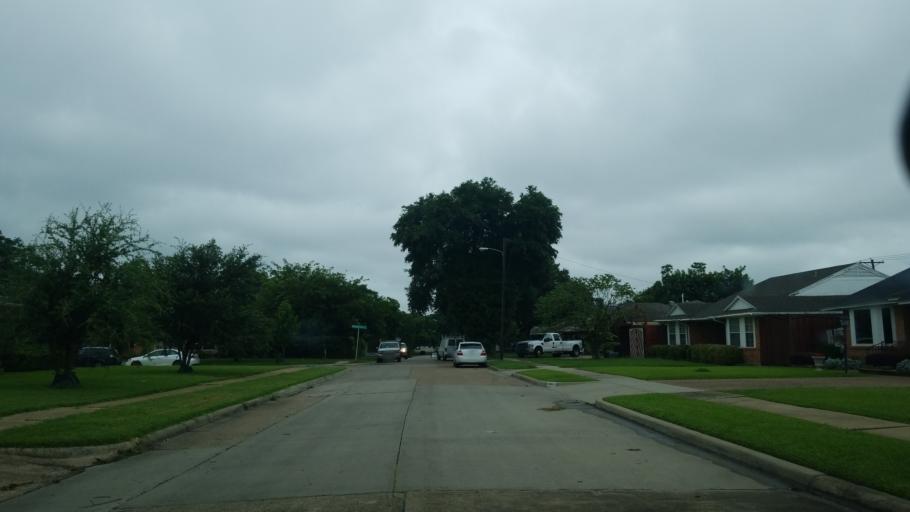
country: US
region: Texas
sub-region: Dallas County
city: Farmers Branch
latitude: 32.8913
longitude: -96.8814
